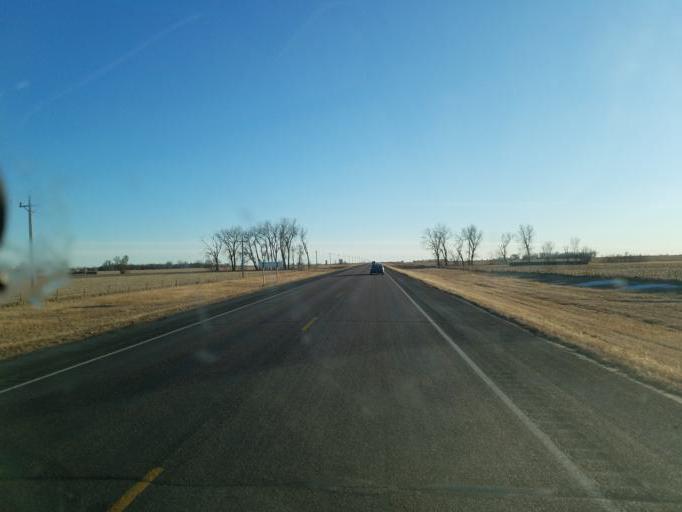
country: US
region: South Dakota
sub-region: Hutchinson County
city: Parkston
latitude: 43.1967
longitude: -97.9719
